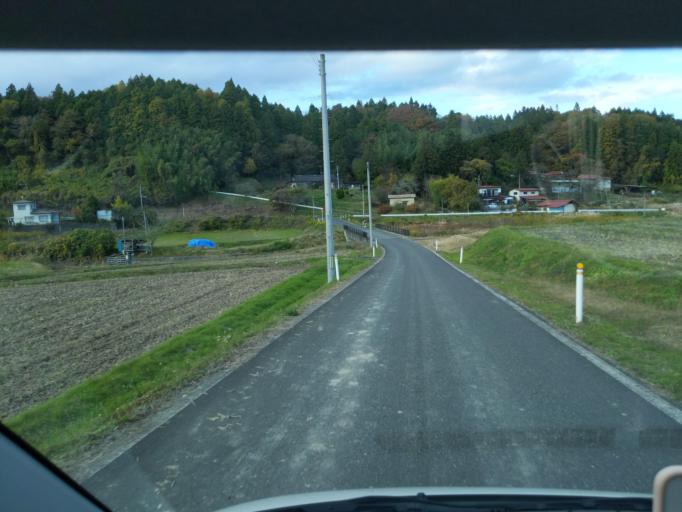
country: JP
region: Iwate
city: Ichinoseki
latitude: 38.8995
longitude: 141.1718
